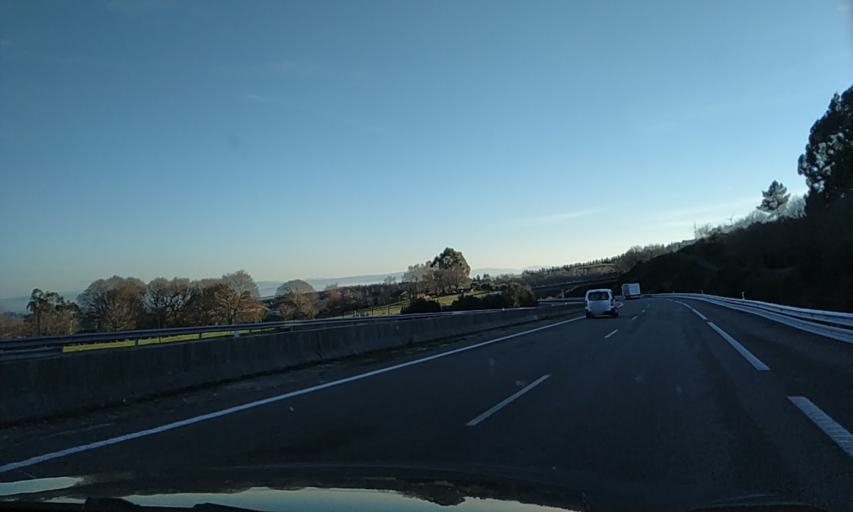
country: ES
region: Galicia
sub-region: Provincia de Pontevedra
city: Dozon
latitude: 42.5475
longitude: -8.0192
